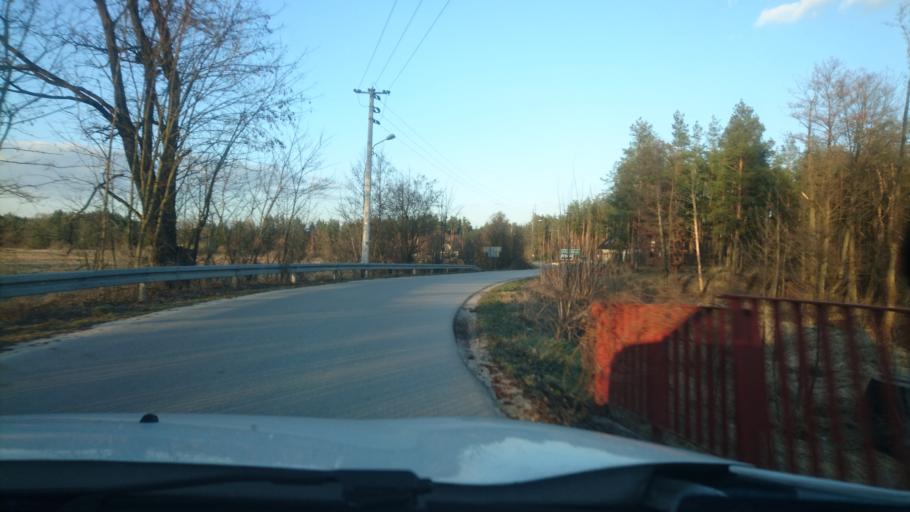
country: PL
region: Swietokrzyskie
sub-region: Powiat kielecki
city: Pierzchnica
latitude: 50.7778
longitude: 20.7089
